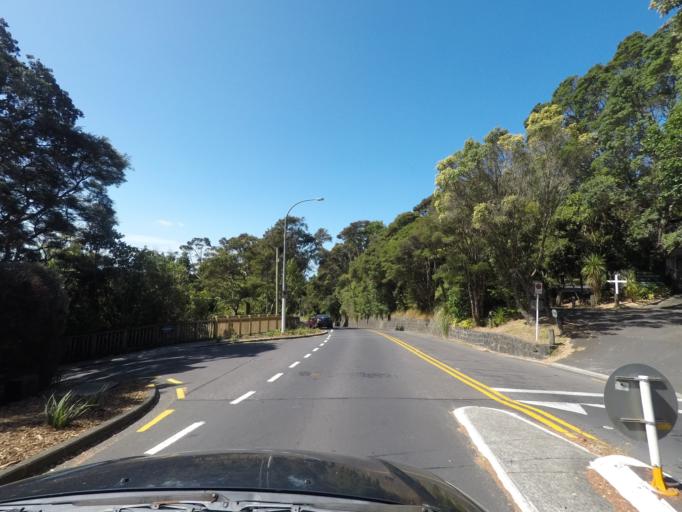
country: NZ
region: Auckland
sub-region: Auckland
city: Titirangi
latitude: -36.9378
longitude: 174.6542
